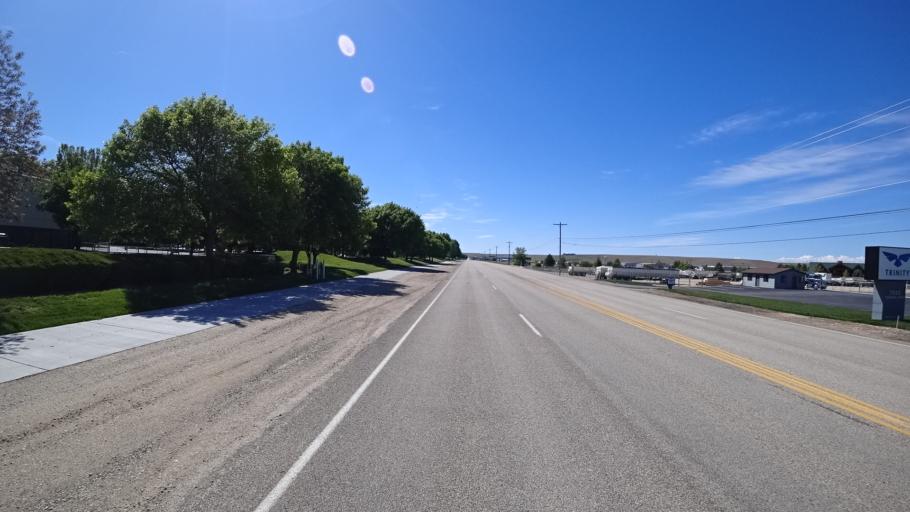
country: US
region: Idaho
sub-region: Ada County
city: Boise
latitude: 43.5327
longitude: -116.1520
